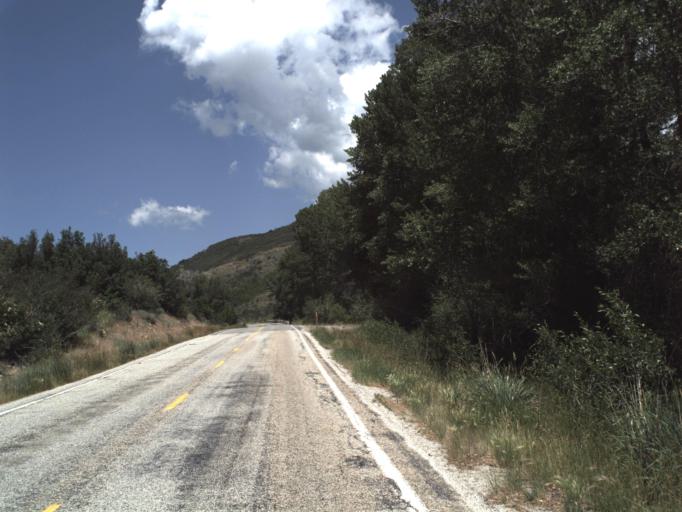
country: US
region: Utah
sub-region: Weber County
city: Wolf Creek
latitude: 41.3542
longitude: -111.5958
